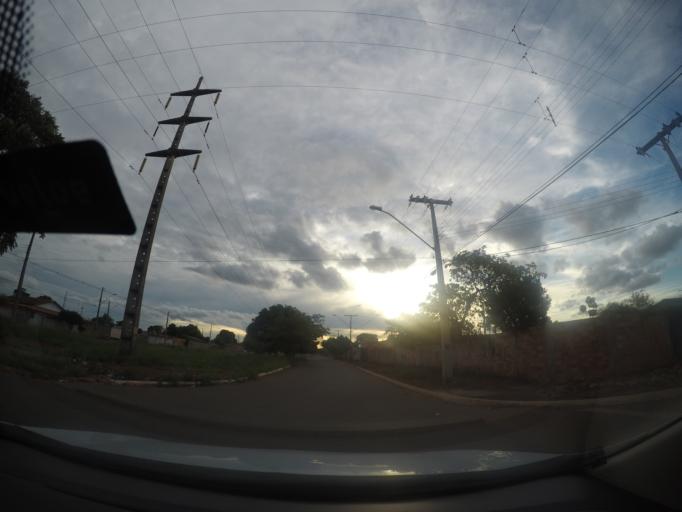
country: BR
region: Goias
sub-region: Goianira
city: Goianira
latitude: -16.5836
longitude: -49.3724
